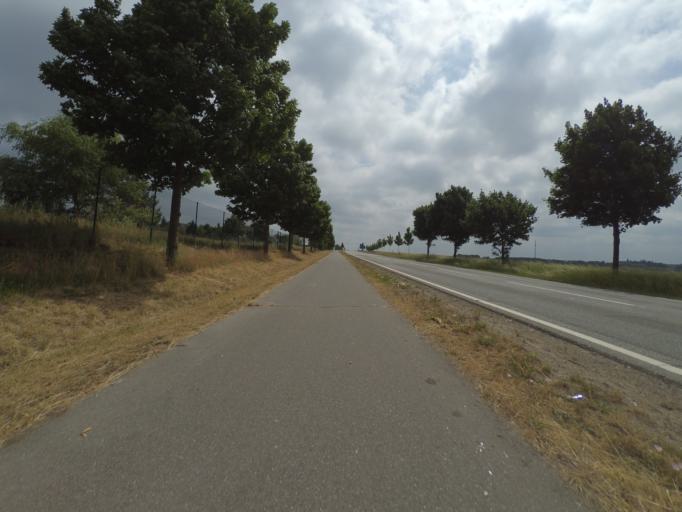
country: DE
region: Mecklenburg-Vorpommern
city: Krakow am See
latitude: 53.6179
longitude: 12.3652
